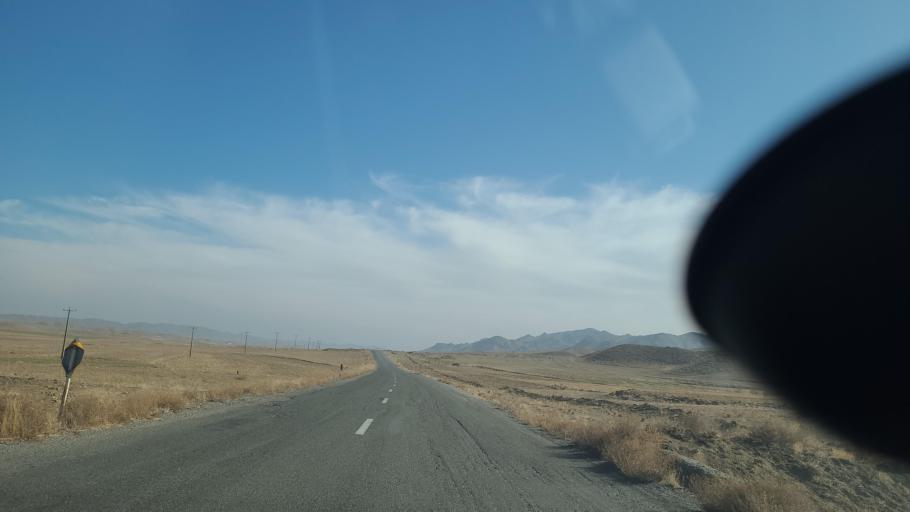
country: IR
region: Razavi Khorasan
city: Fariman
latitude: 35.5874
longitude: 59.6408
